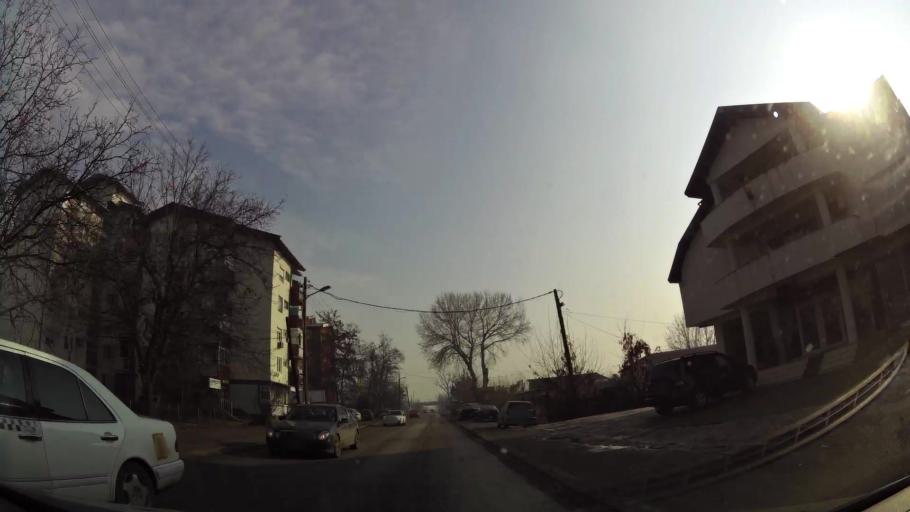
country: MK
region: Kisela Voda
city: Kisela Voda
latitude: 41.9920
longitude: 21.5085
